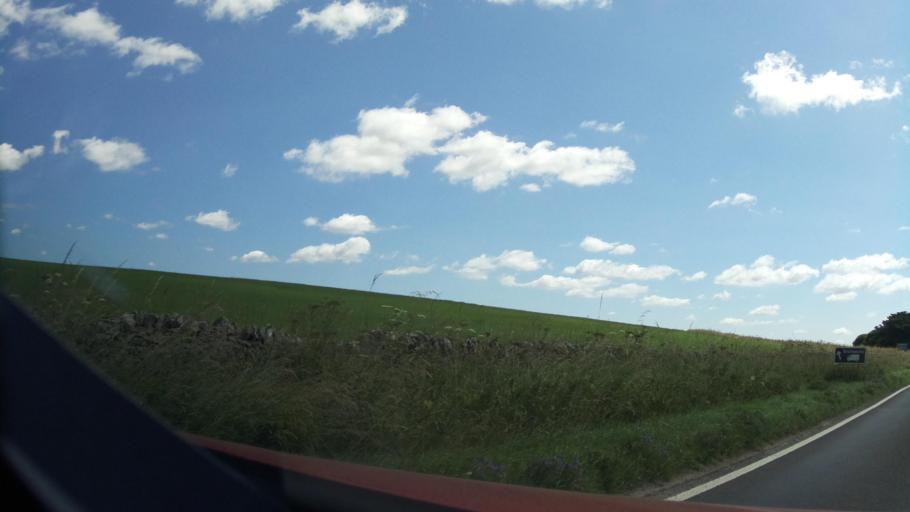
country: GB
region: England
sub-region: Derbyshire
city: Bakewell
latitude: 53.1487
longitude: -1.7658
